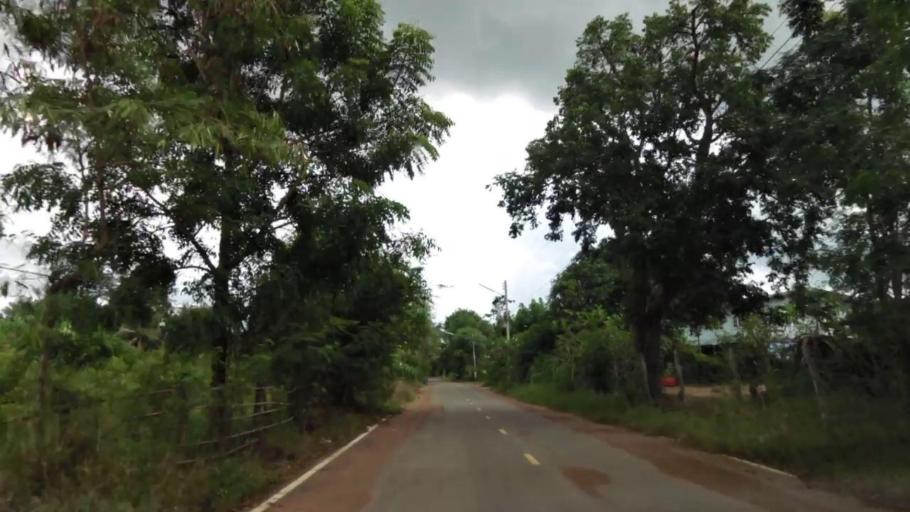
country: TH
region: Nakhon Sawan
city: Phai Sali
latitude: 15.6051
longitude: 100.6604
